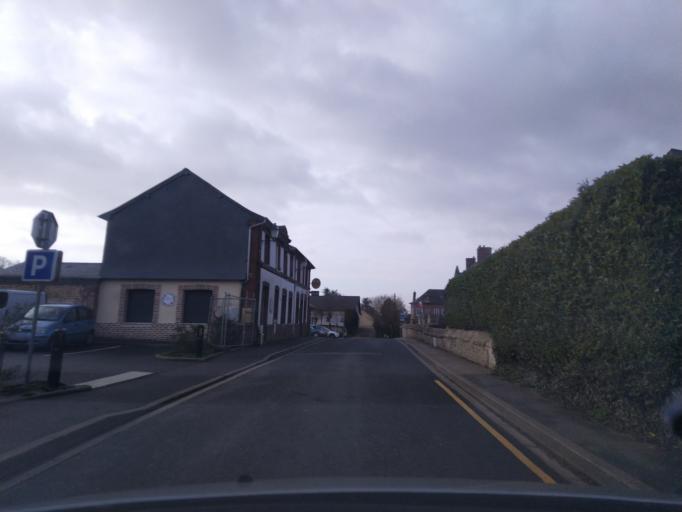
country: FR
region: Haute-Normandie
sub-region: Departement de la Seine-Maritime
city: Roumare
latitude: 49.5106
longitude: 0.9770
